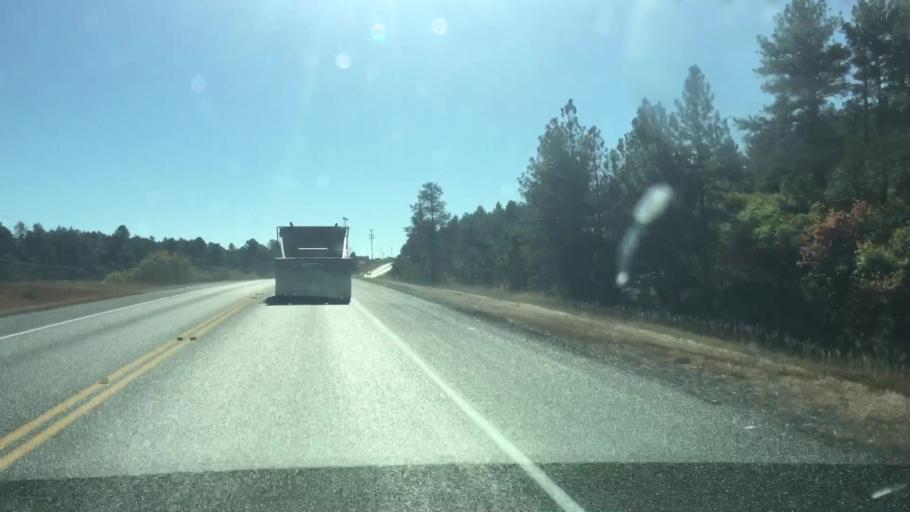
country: US
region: Colorado
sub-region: Elbert County
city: Ponderosa Park
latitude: 39.3741
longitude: -104.6874
